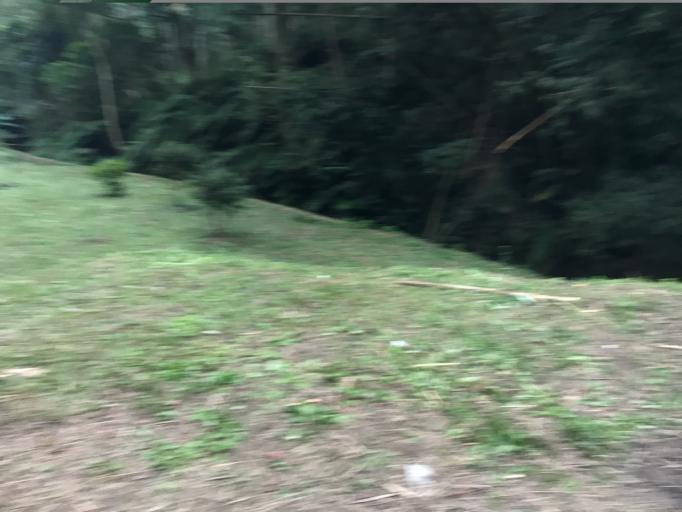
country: TW
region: Taiwan
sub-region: Miaoli
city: Miaoli
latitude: 24.6241
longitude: 120.9566
